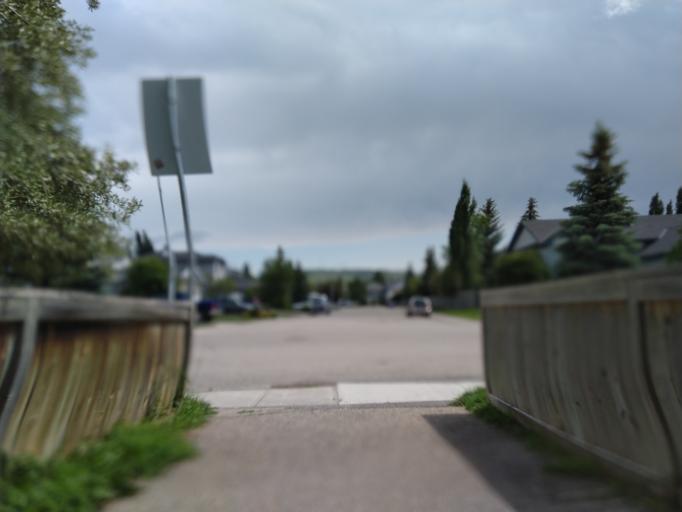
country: CA
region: Alberta
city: Cochrane
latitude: 51.1853
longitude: -114.4990
